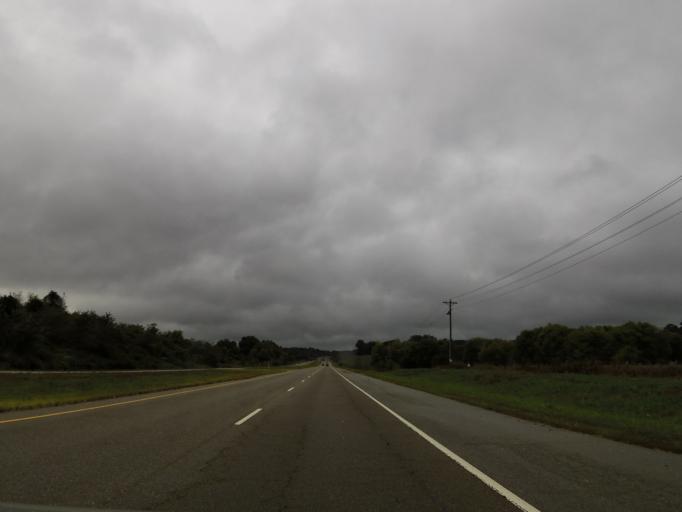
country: US
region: Tennessee
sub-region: Loudon County
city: Greenback
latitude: 35.7365
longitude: -84.1771
